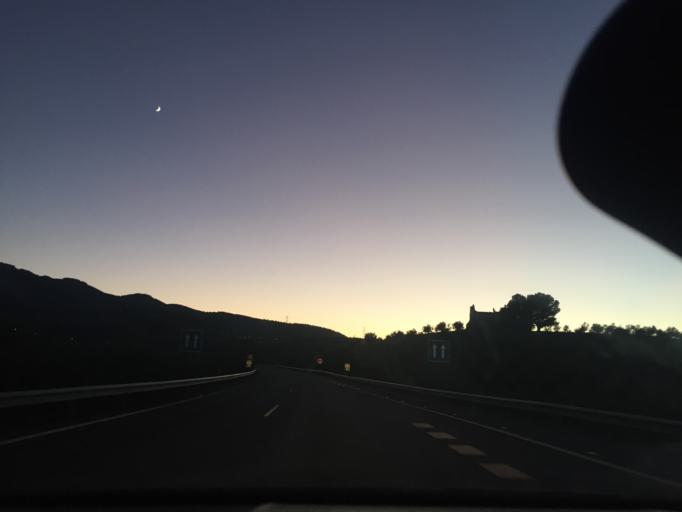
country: ES
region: Andalusia
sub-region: Provincia de Jaen
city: Jaen
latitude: 37.8024
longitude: -3.8191
